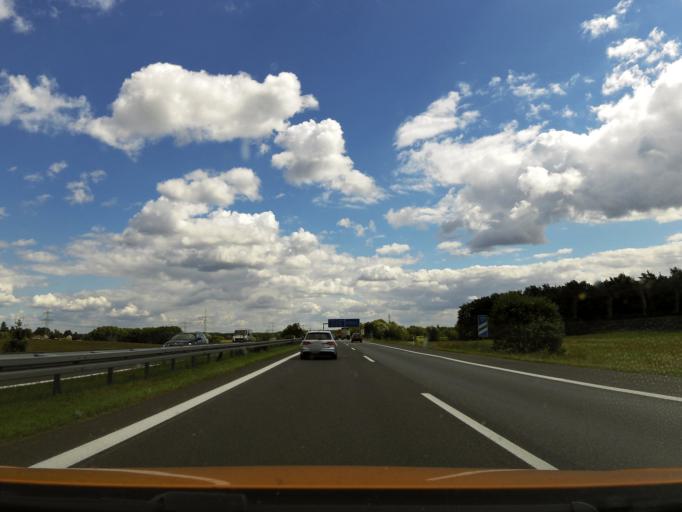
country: DE
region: Brandenburg
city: Glienicke
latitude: 52.6816
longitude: 13.3618
